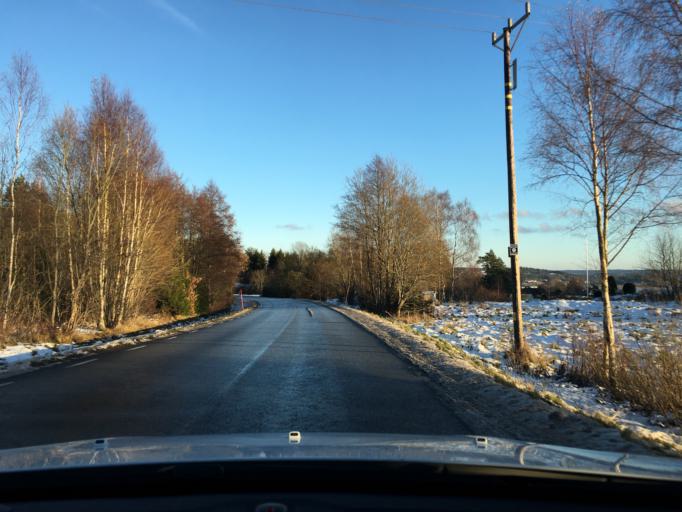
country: SE
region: Vaestra Goetaland
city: Svanesund
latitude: 58.1388
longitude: 11.7769
